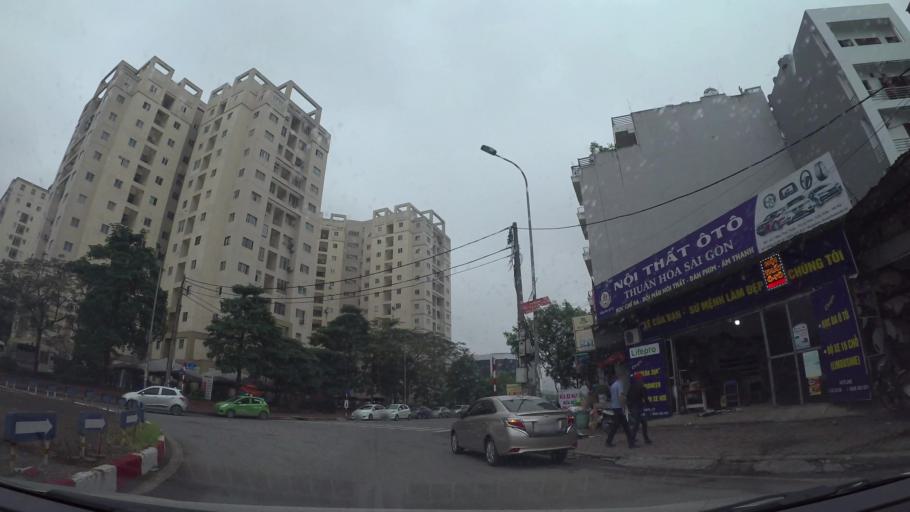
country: VN
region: Ha Noi
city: Thanh Xuan
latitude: 21.0104
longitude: 105.7904
